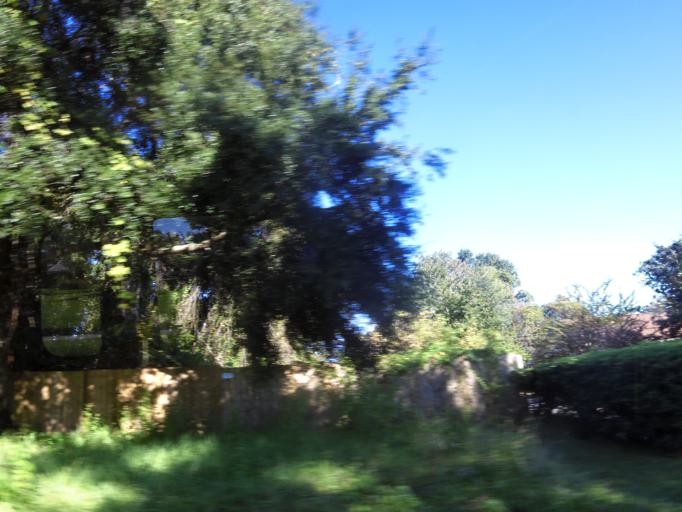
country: US
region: Florida
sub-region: Duval County
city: Neptune Beach
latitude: 30.3022
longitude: -81.4380
